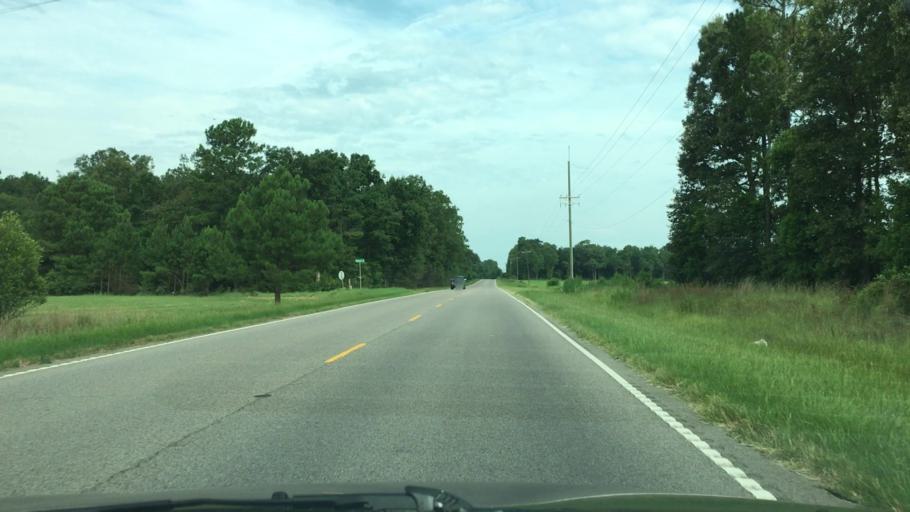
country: US
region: South Carolina
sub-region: Lexington County
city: Leesville
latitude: 33.6821
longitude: -81.4472
